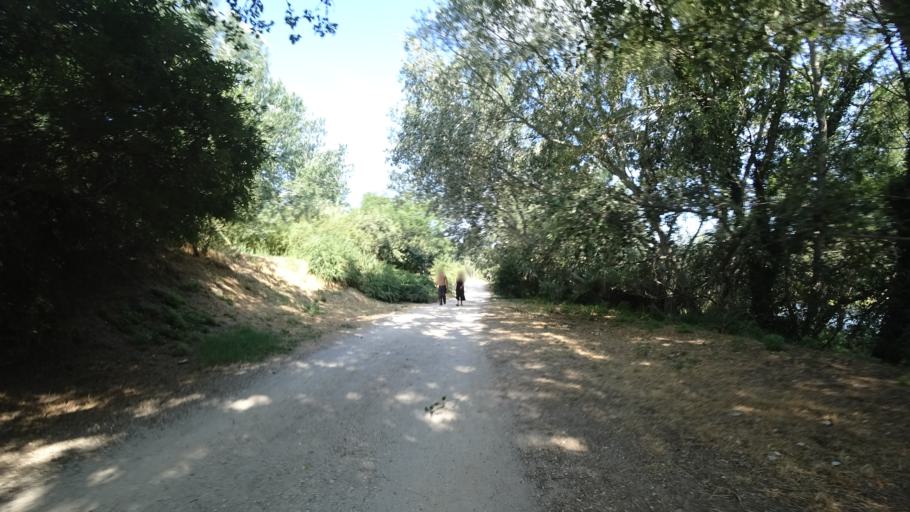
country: FR
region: Languedoc-Roussillon
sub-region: Departement des Pyrenees-Orientales
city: Rivesaltes
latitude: 42.7716
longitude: 2.8709
